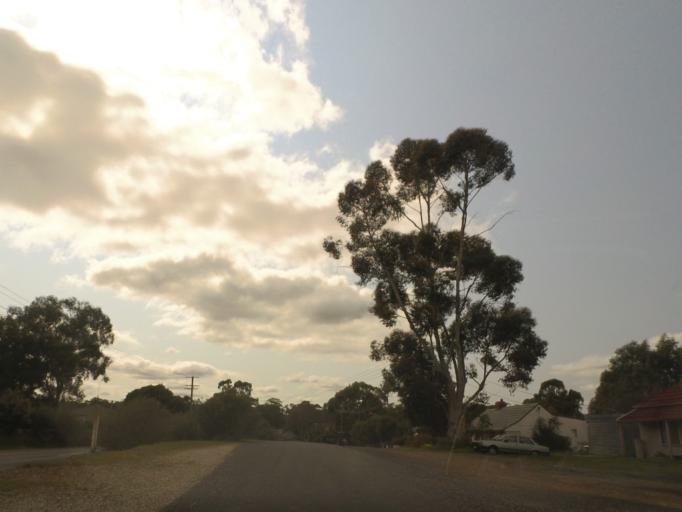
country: AU
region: Victoria
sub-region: Murrindindi
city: Kinglake West
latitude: -37.0936
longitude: 145.1033
